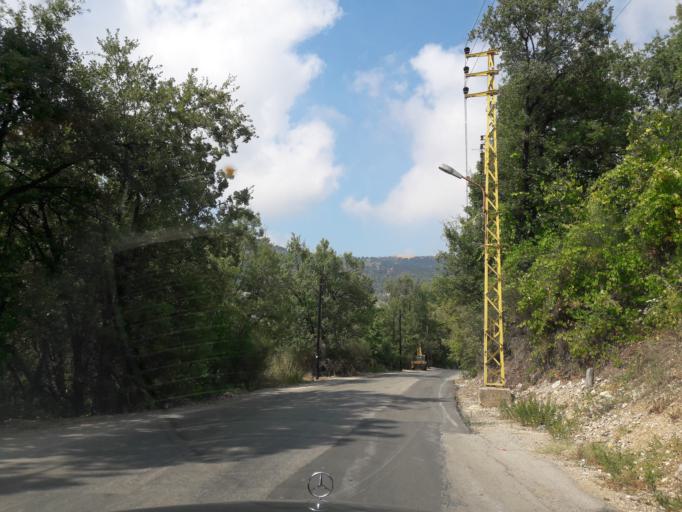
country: LB
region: Mont-Liban
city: Djounie
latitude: 33.9599
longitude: 35.7787
